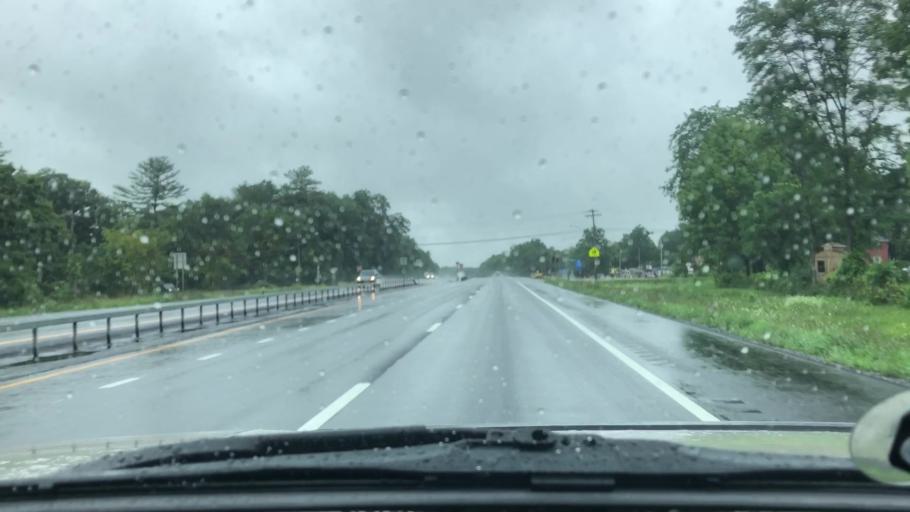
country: US
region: New York
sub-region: Greene County
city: Cairo
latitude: 42.3000
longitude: -73.9926
